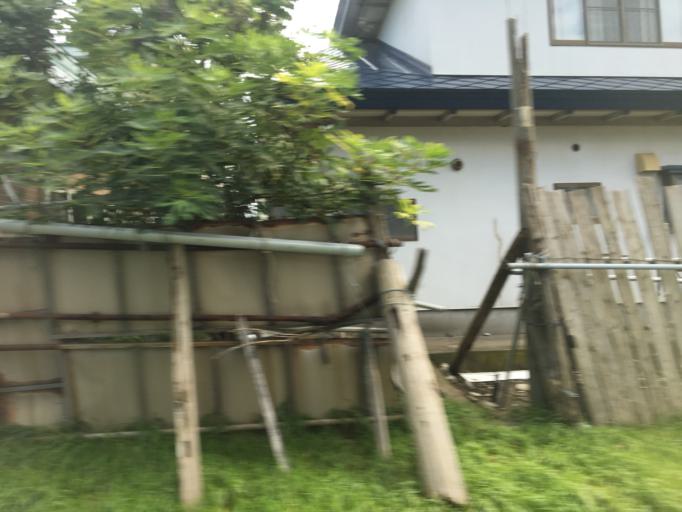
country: JP
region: Aomori
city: Shimokizukuri
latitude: 40.7631
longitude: 140.1637
